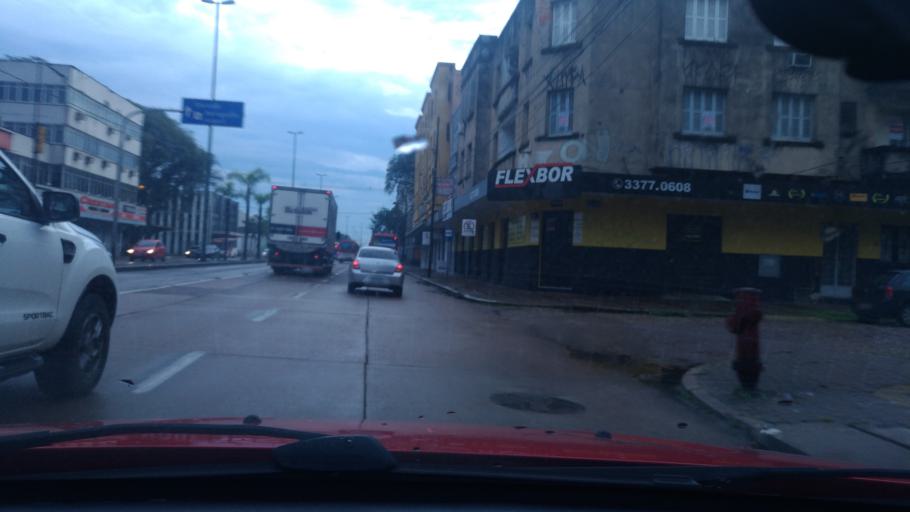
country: BR
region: Rio Grande do Sul
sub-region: Porto Alegre
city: Porto Alegre
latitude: -30.0098
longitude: -51.2023
